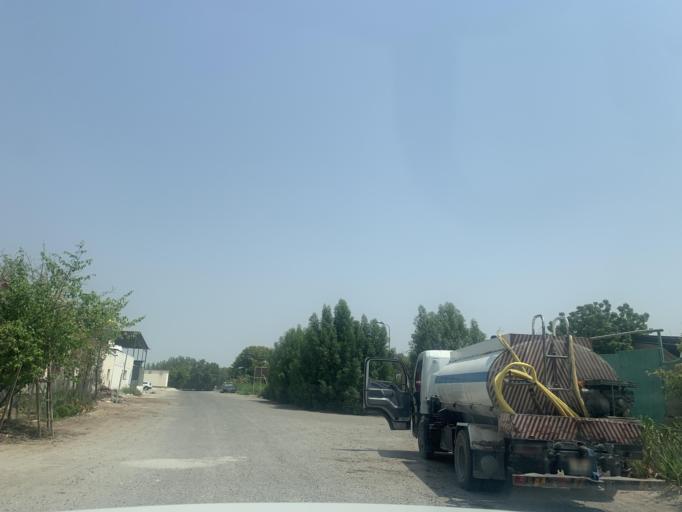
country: BH
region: Central Governorate
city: Madinat Hamad
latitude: 26.1416
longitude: 50.4761
